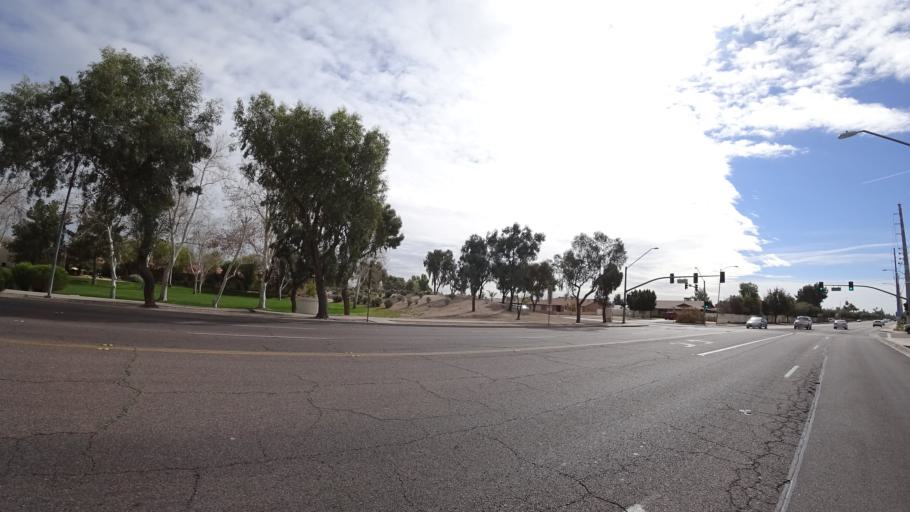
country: US
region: Arizona
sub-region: Maricopa County
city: Peoria
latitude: 33.6329
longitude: -112.1858
